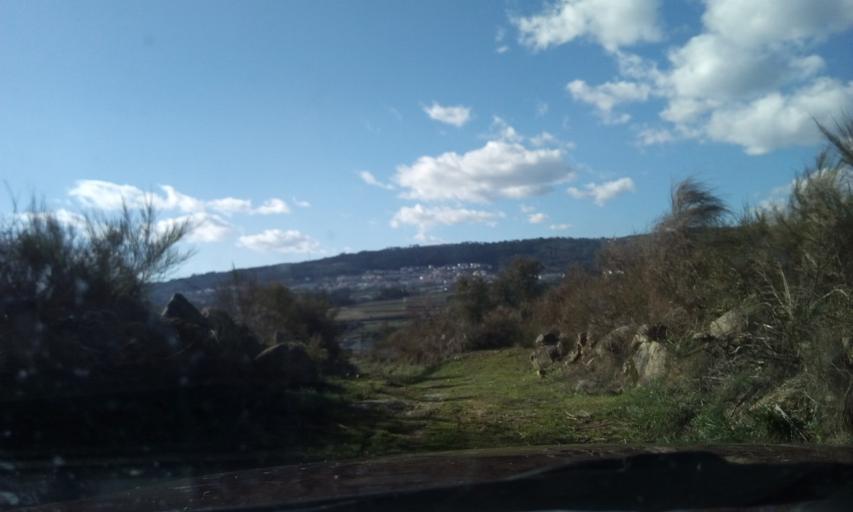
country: PT
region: Guarda
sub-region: Fornos de Algodres
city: Fornos de Algodres
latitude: 40.6080
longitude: -7.5172
